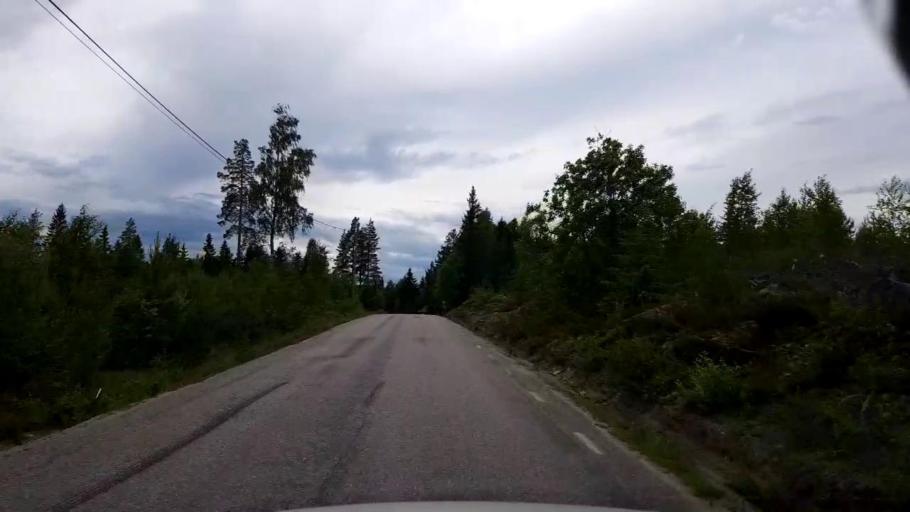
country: SE
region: Gaevleborg
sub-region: Hudiksvalls Kommun
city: Delsbo
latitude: 61.8065
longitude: 16.4695
